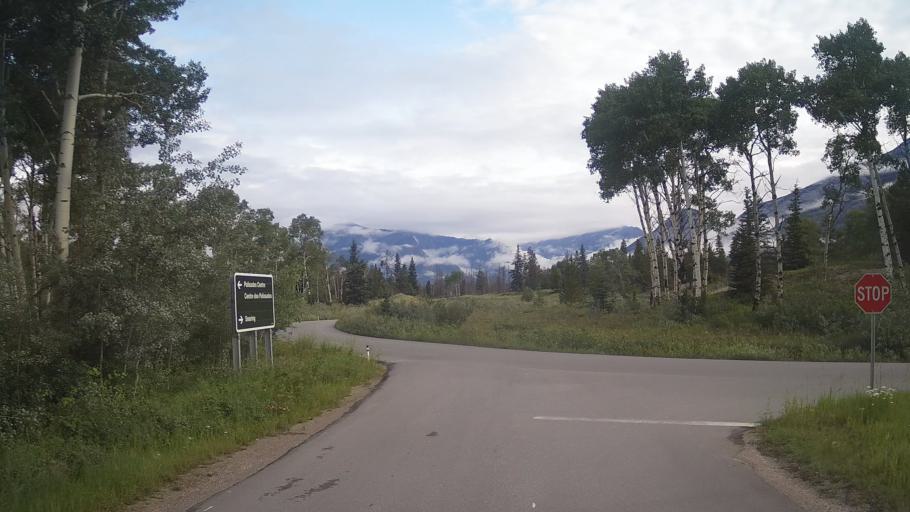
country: CA
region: Alberta
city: Jasper Park Lodge
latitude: 52.9703
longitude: -118.0599
